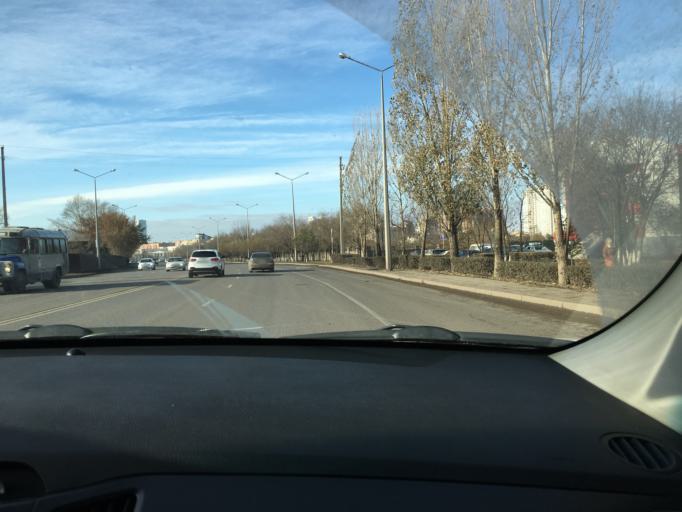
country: KZ
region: Astana Qalasy
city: Astana
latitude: 51.1567
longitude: 71.4514
